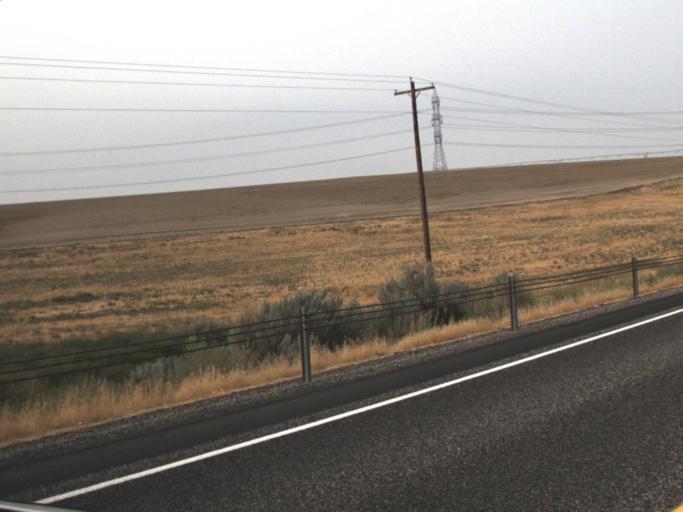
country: US
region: Washington
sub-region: Benton County
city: Prosser
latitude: 46.0773
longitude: -119.6021
